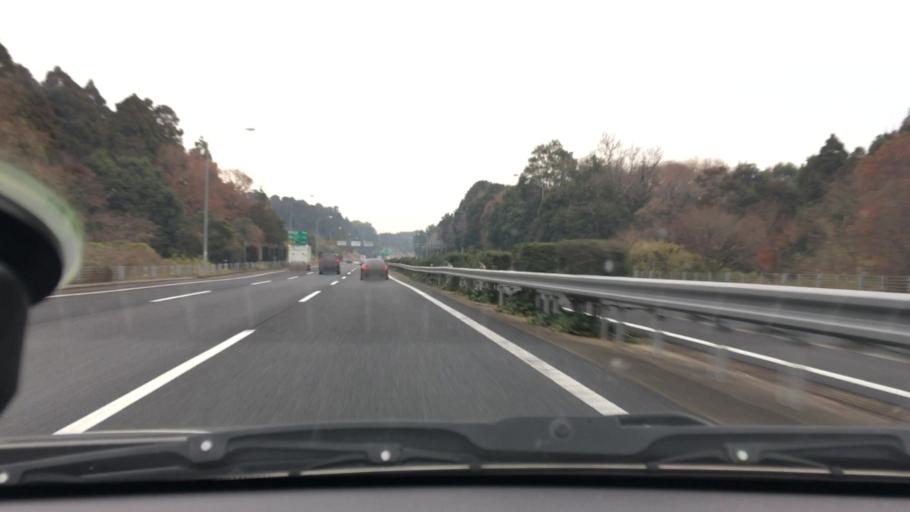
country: JP
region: Chiba
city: Narita
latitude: 35.7542
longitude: 140.3187
